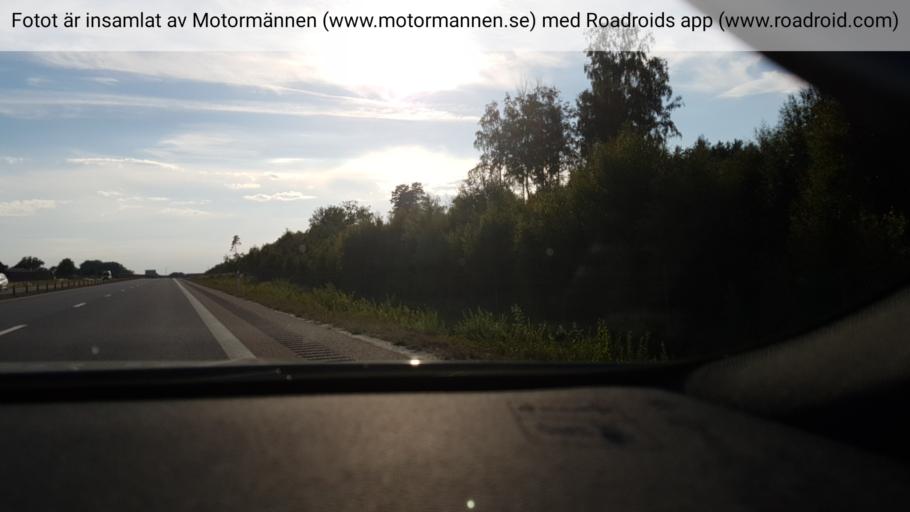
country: SE
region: Vaestra Goetaland
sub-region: Skara Kommun
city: Axvall
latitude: 58.3949
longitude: 13.5158
